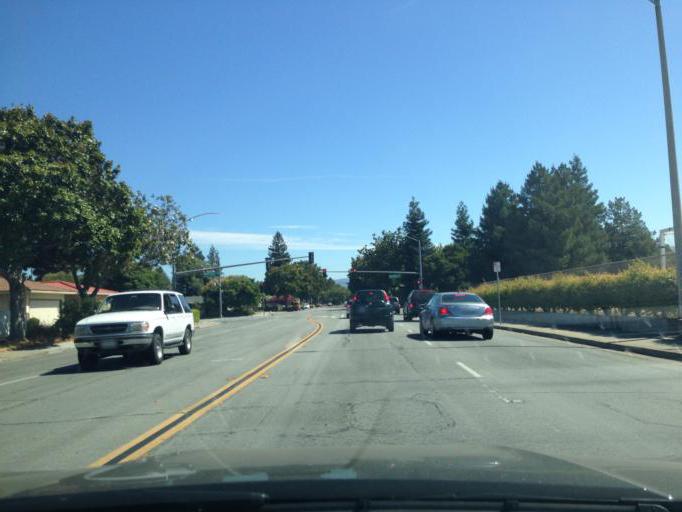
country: US
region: California
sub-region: Santa Clara County
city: Sunnyvale
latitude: 37.3604
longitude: -122.0502
